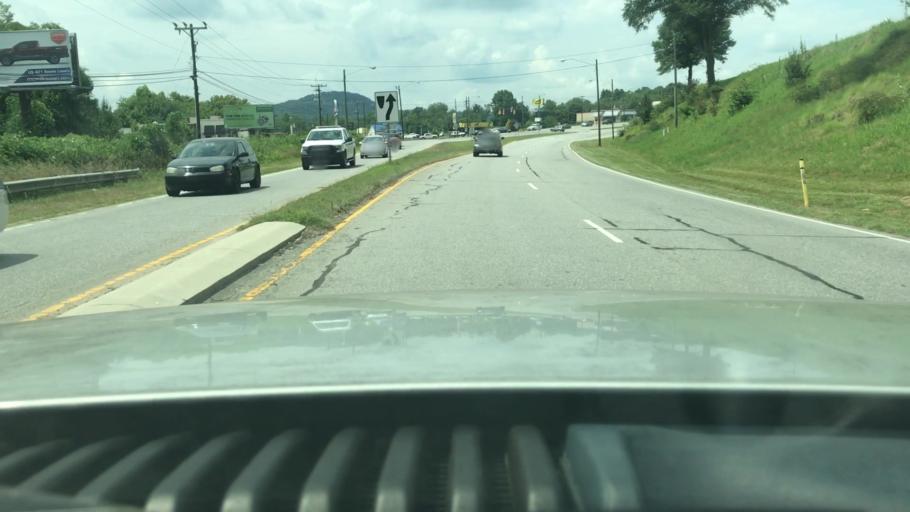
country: US
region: North Carolina
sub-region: Wilkes County
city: Wilkesboro
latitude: 36.1511
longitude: -81.1773
